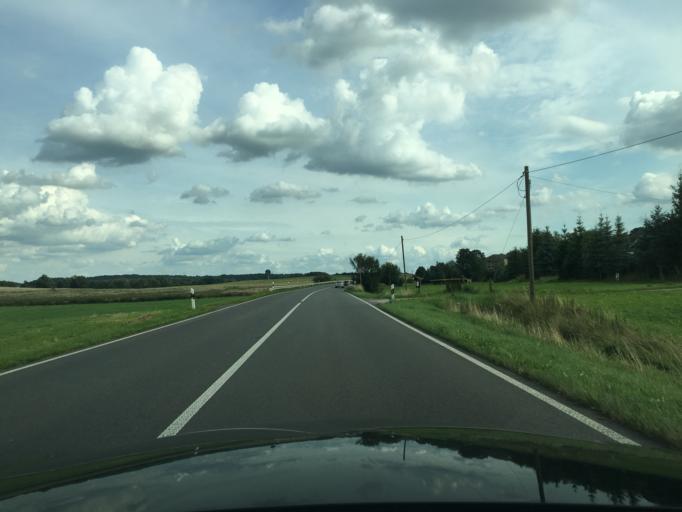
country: DE
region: Mecklenburg-Vorpommern
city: Penzlin
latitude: 53.4909
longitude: 13.0713
